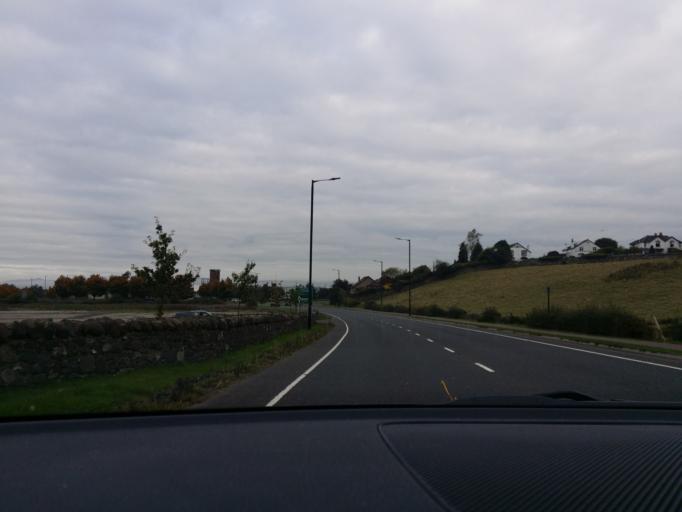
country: GB
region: Scotland
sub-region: Stirling
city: Stirling
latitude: 56.1228
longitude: -3.9522
